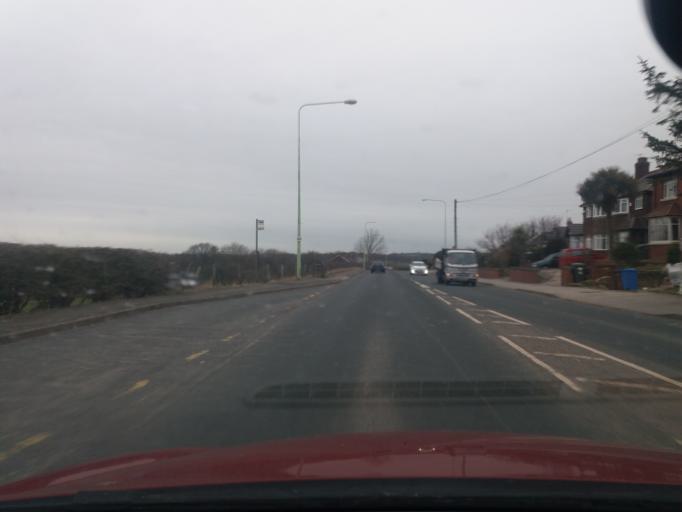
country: GB
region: England
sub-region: Lancashire
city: Chorley
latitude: 53.6688
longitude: -2.6156
